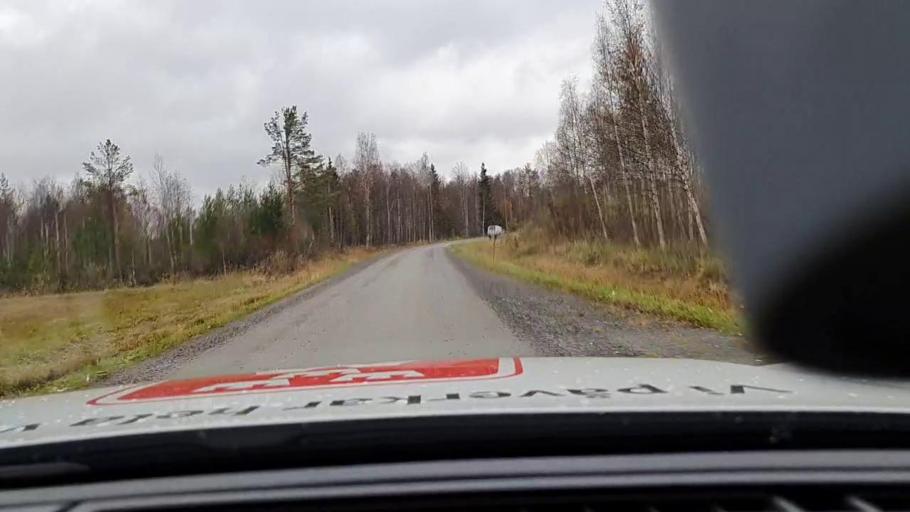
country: SE
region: Norrbotten
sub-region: Haparanda Kommun
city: Haparanda
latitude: 65.9707
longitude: 23.9422
